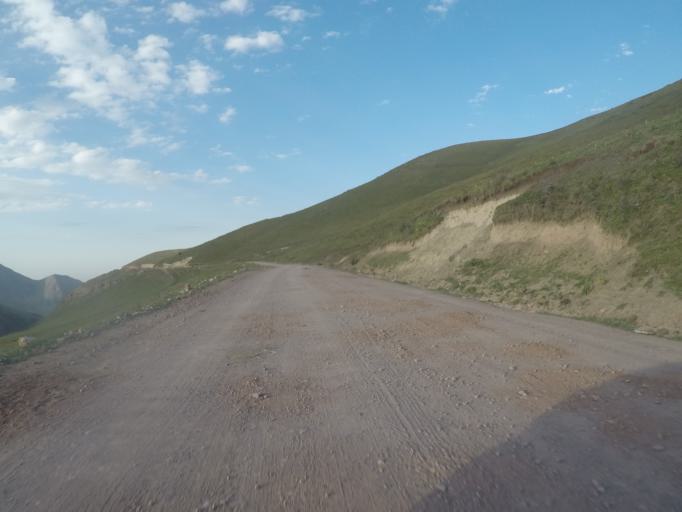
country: KG
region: Chuy
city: Bishkek
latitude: 42.6403
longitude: 74.6414
